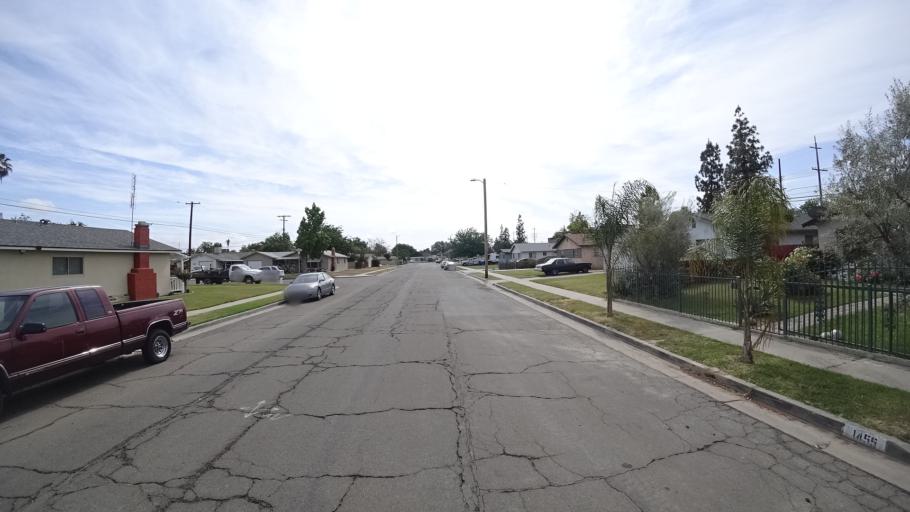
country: US
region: California
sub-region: Kings County
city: Hanford
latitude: 36.3139
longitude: -119.6682
